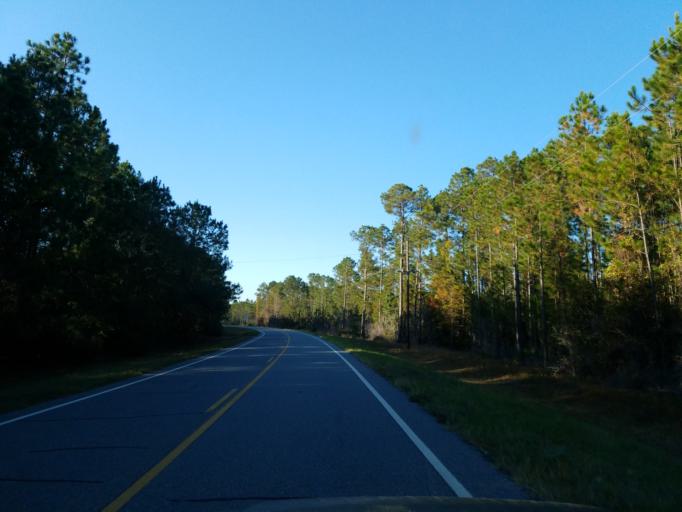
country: US
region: Georgia
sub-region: Lanier County
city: Lakeland
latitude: 30.8952
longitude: -83.0581
